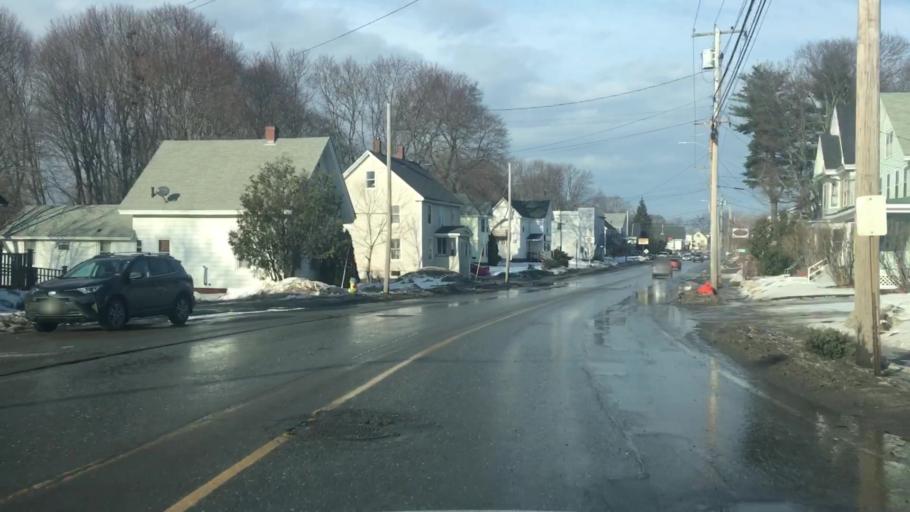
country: US
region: Maine
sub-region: Penobscot County
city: Bangor
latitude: 44.7719
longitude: -68.7803
